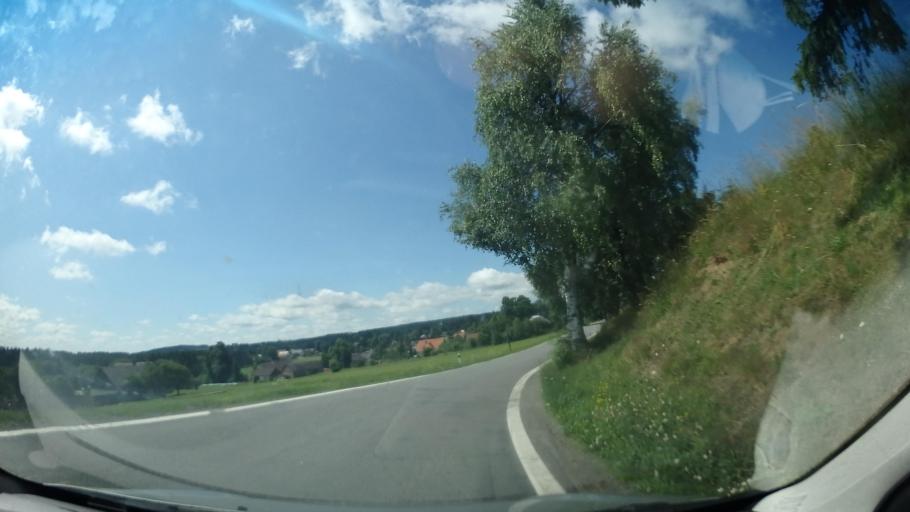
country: CZ
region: Vysocina
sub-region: Okres Zd'ar nad Sazavou
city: Nove Mesto na Morave
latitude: 49.6198
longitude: 16.0371
